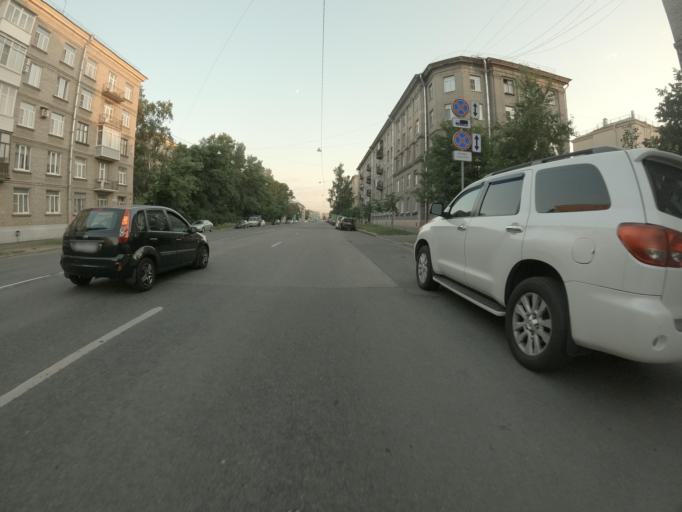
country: RU
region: St.-Petersburg
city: Avtovo
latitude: 59.8793
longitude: 30.2737
